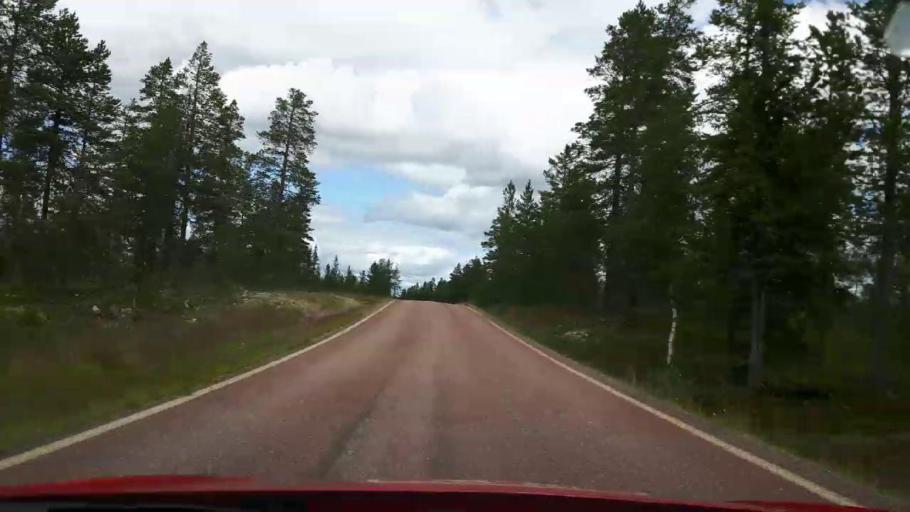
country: NO
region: Hedmark
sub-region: Trysil
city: Innbygda
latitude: 61.9227
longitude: 13.0169
